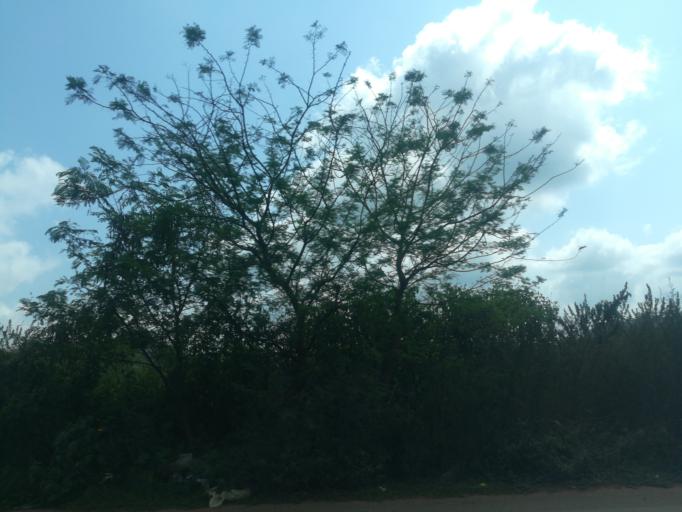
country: NG
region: Oyo
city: Moniya
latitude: 7.5691
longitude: 3.9144
